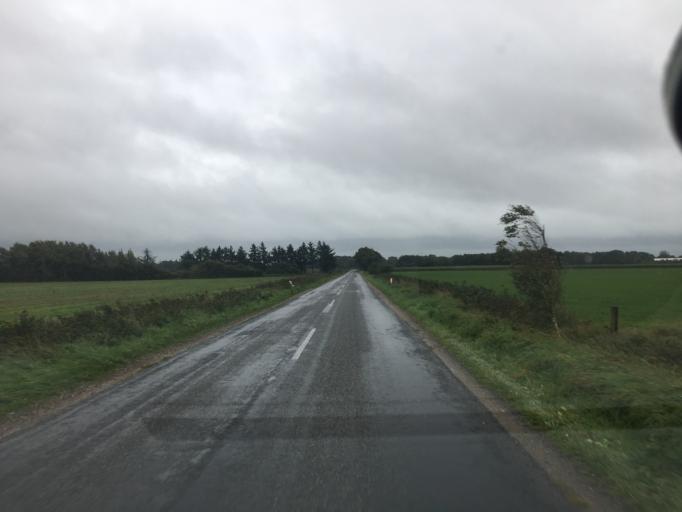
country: DE
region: Schleswig-Holstein
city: Bramstedtlund
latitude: 54.9658
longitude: 9.0480
